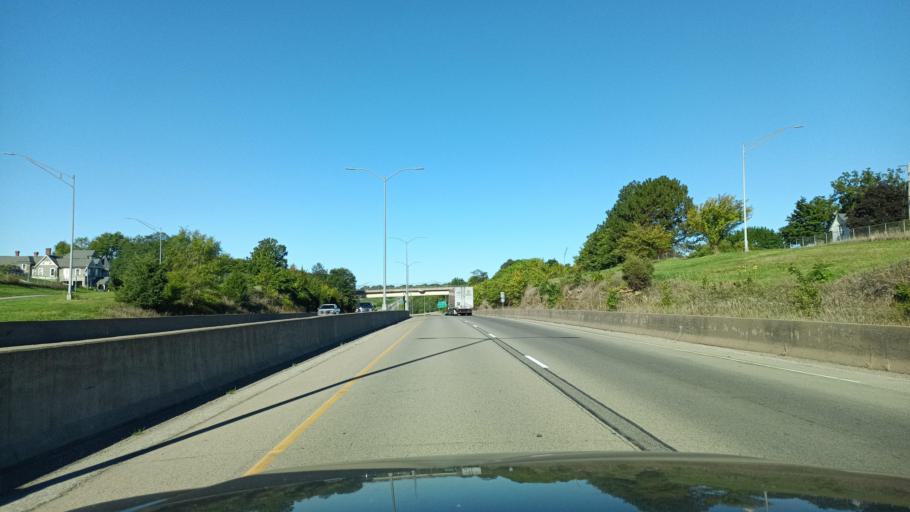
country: US
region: Iowa
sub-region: Des Moines County
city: Burlington
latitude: 40.8154
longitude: -91.1078
